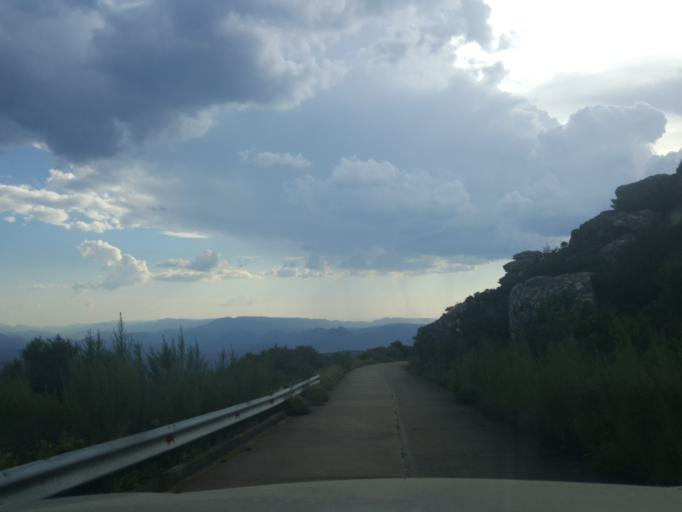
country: ZA
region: Limpopo
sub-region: Mopani District Municipality
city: Hoedspruit
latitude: -24.5521
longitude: 30.8721
